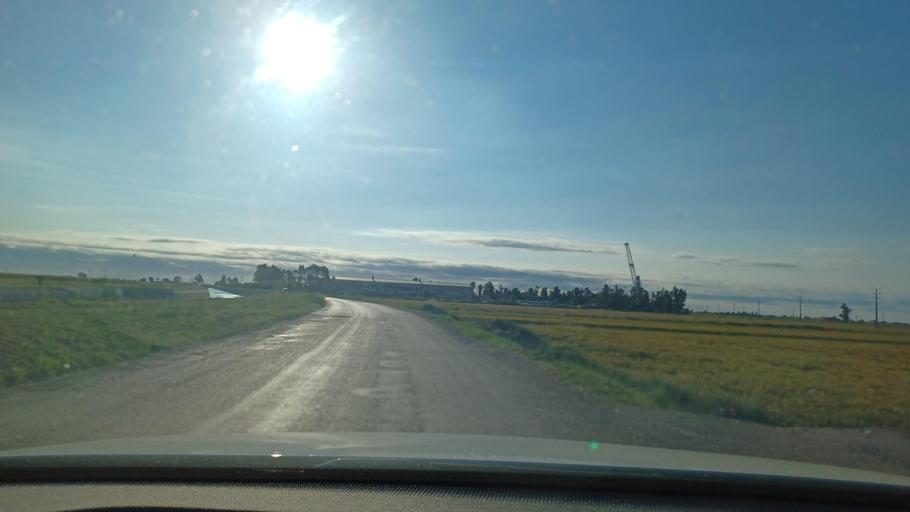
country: ES
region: Catalonia
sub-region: Provincia de Tarragona
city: Amposta
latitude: 40.7016
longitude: 0.5987
